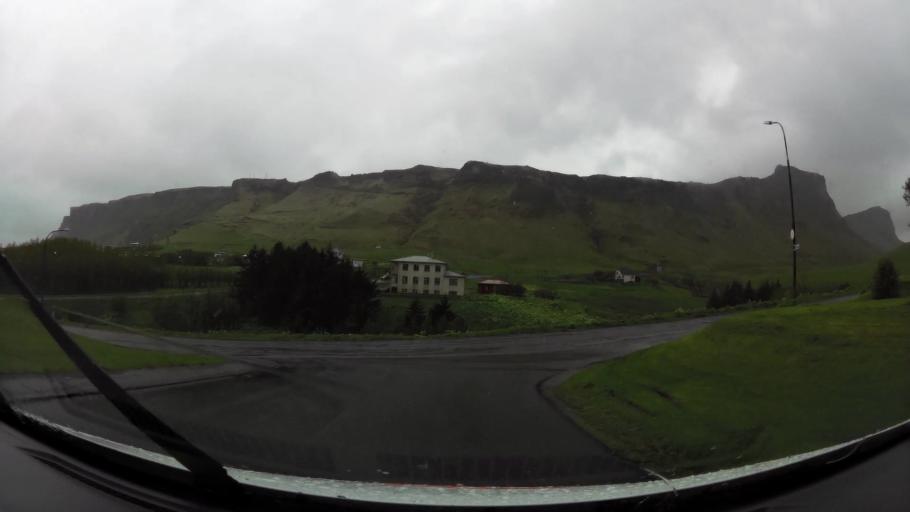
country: IS
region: South
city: Vestmannaeyjar
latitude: 63.4213
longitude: -19.0083
